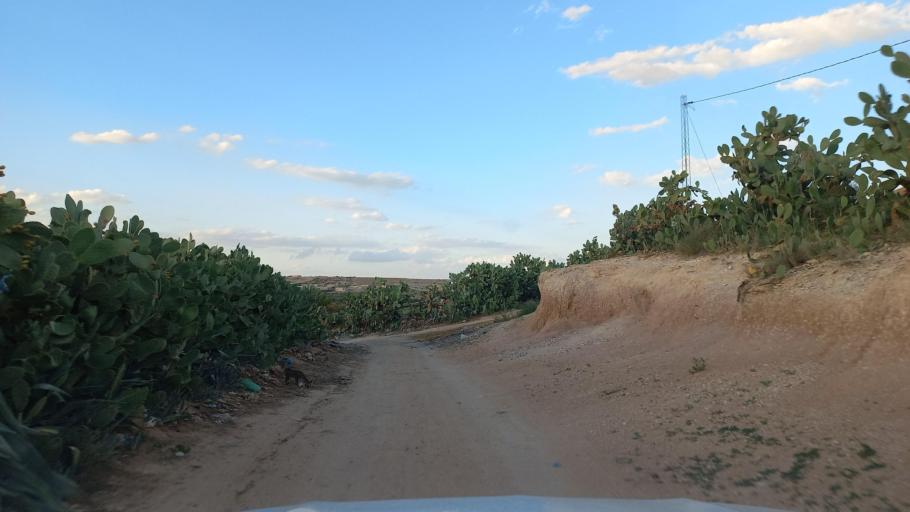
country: TN
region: Al Qasrayn
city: Sbiba
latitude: 35.3765
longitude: 9.0567
